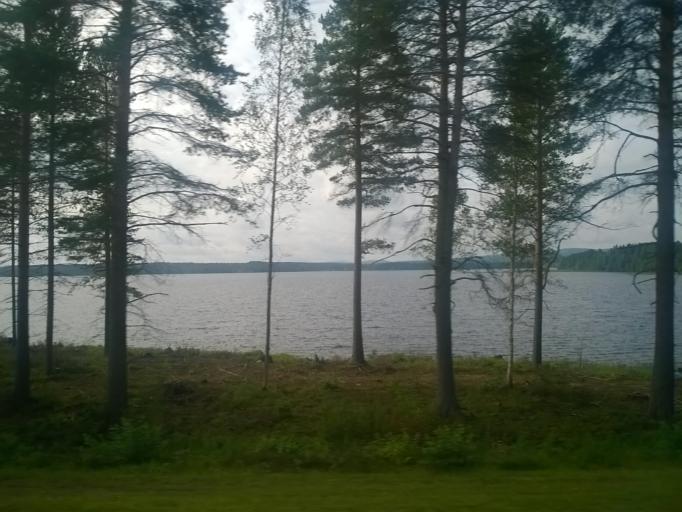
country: FI
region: Kainuu
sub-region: Kajaani
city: Sotkamo
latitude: 64.1335
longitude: 28.3514
